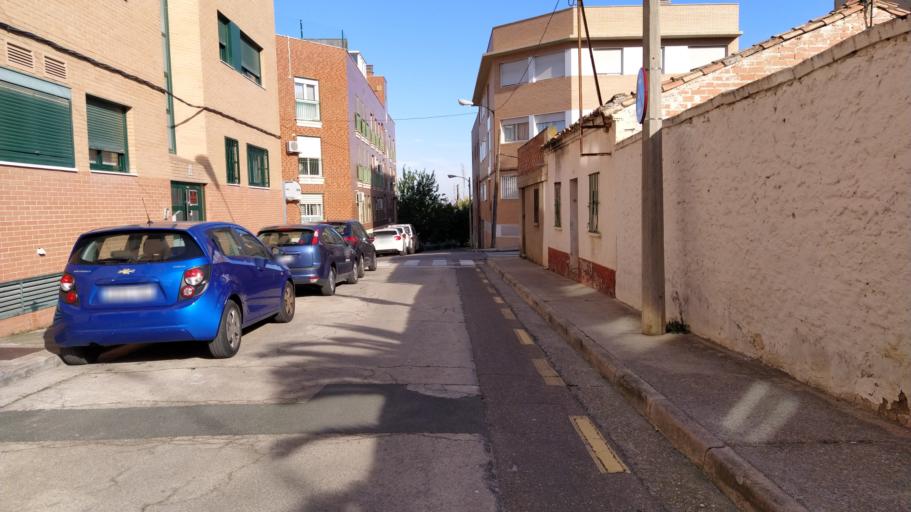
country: ES
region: Aragon
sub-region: Provincia de Zaragoza
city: Oliver-Valdefierro, Oliver, Valdefierro
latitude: 41.6390
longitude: -0.9360
